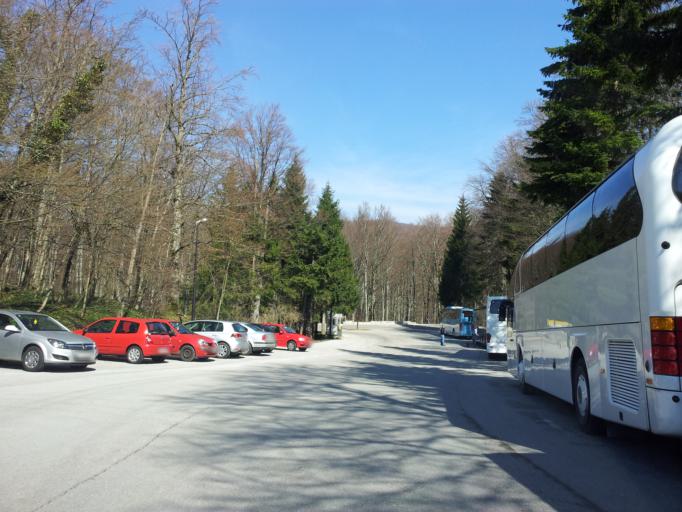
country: HR
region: Licko-Senjska
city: Jezerce
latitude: 44.8846
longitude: 15.6190
